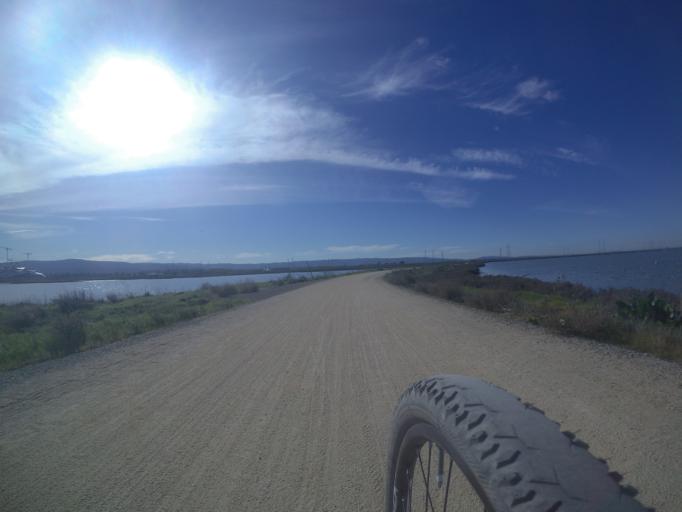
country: US
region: California
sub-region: Santa Clara County
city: Mountain View
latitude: 37.4337
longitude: -122.0617
